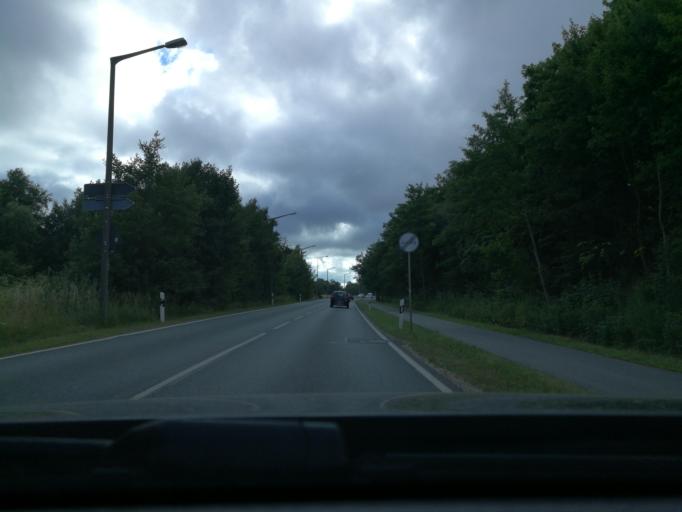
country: DE
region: Bavaria
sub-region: Regierungsbezirk Mittelfranken
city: Wetzendorf
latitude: 49.5226
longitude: 11.0249
